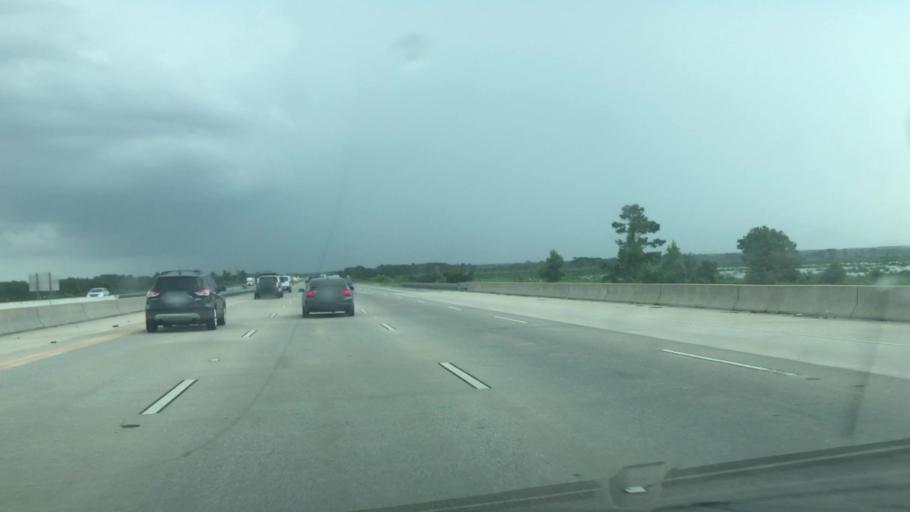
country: US
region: Georgia
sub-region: McIntosh County
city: Darien
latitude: 31.3632
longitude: -81.4580
